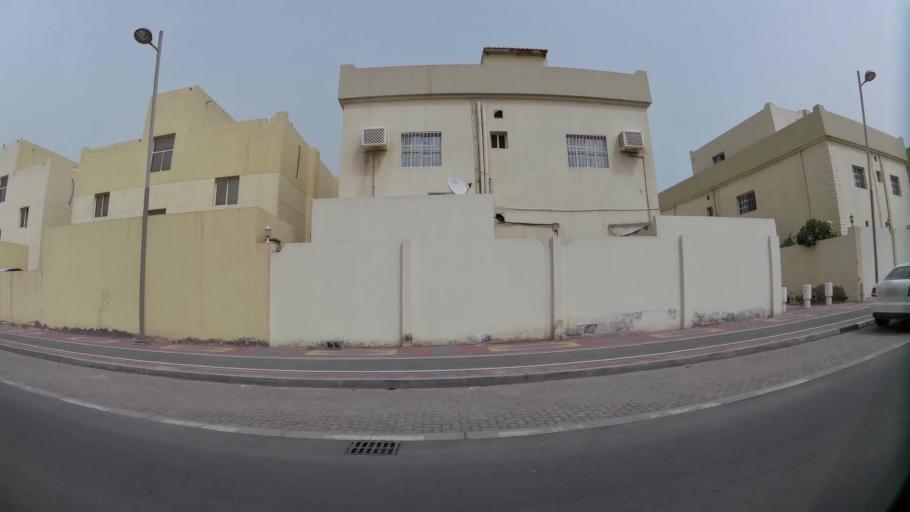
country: QA
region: Baladiyat ad Dawhah
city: Doha
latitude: 25.2338
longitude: 51.5462
